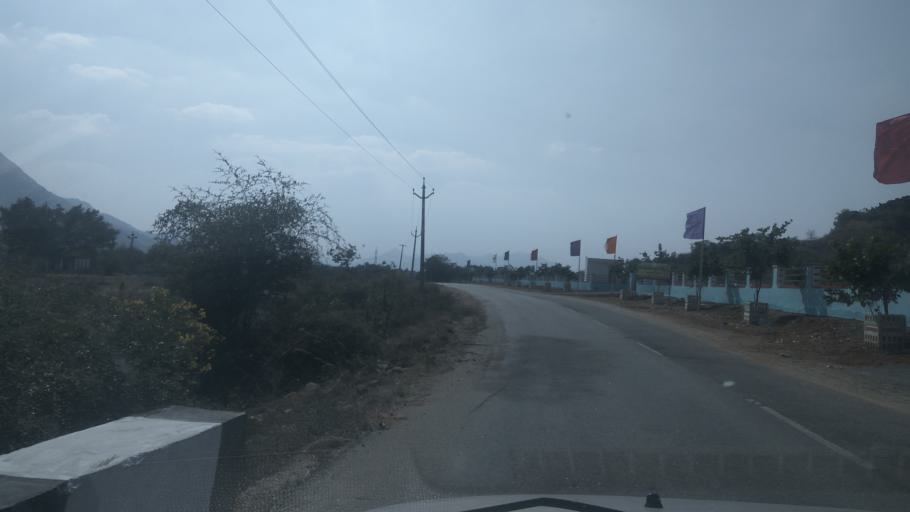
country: IN
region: Andhra Pradesh
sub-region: Chittoor
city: Renigunta
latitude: 13.5544
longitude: 79.4859
